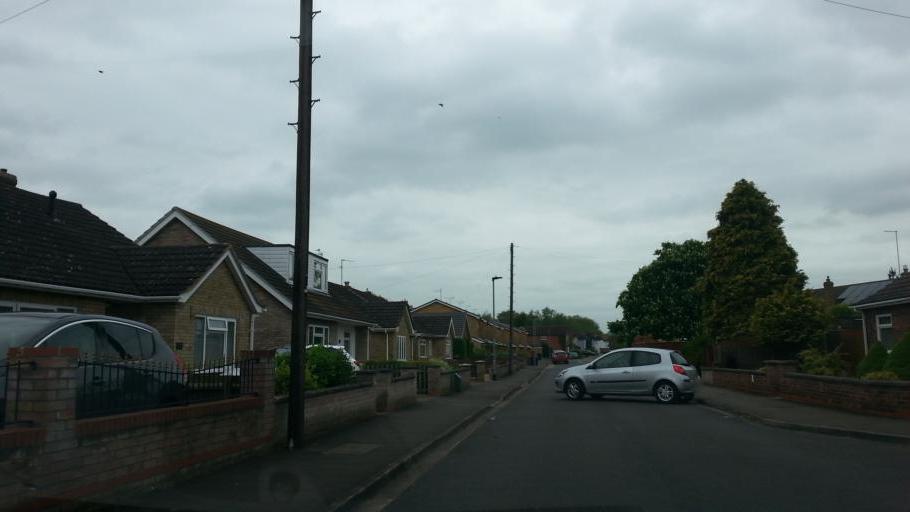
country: GB
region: England
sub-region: Peterborough
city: Peterborough
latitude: 52.5699
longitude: -0.2522
